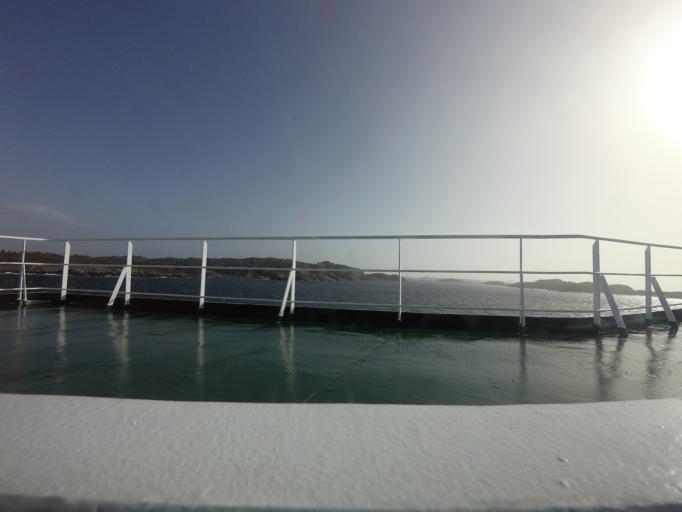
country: NO
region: Hordaland
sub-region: Oygarden
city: Tjeldsto
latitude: 60.6074
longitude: 4.9454
